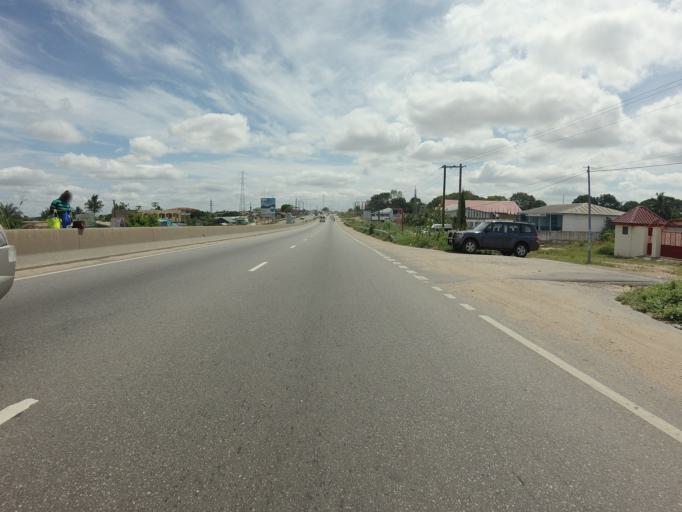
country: GH
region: Central
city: Kasoa
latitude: 5.5305
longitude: -0.4449
